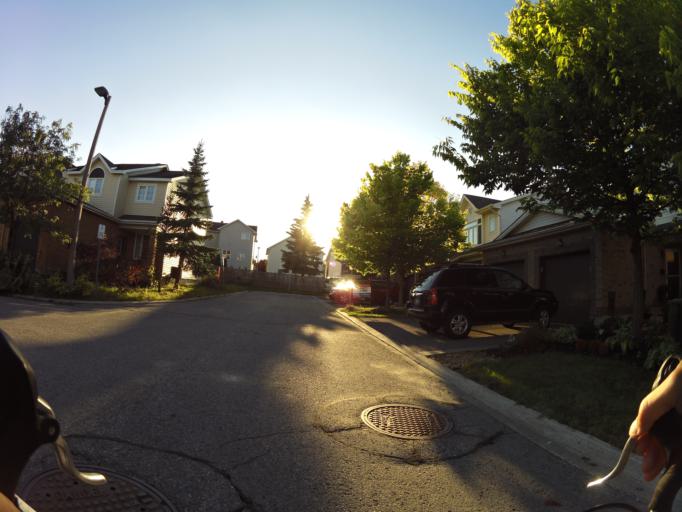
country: CA
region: Ontario
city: Bells Corners
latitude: 45.3544
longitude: -75.9238
